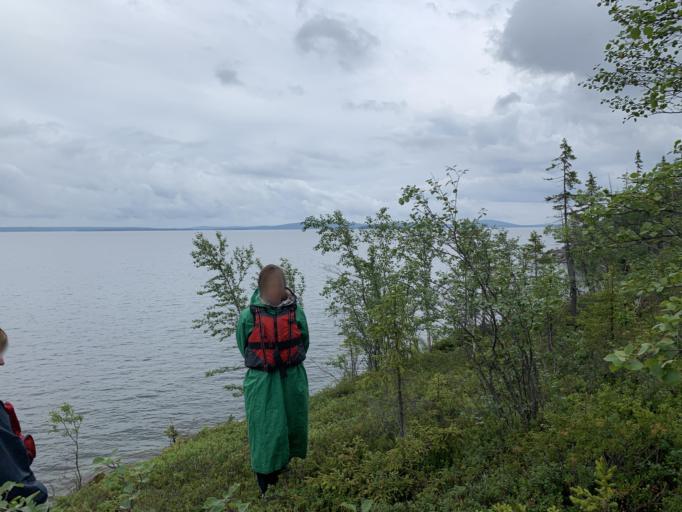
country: RU
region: Murmansk
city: Monchegorsk
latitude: 67.6945
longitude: 33.0607
